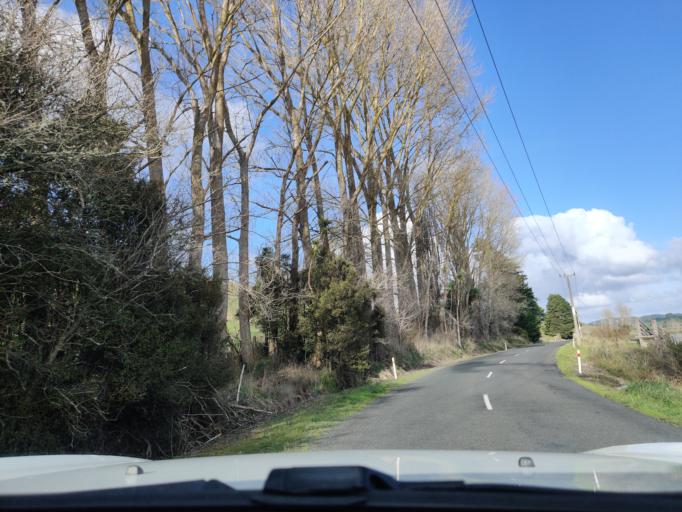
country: NZ
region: Waikato
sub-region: Waikato District
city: Te Kauwhata
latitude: -37.2711
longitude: 175.1997
